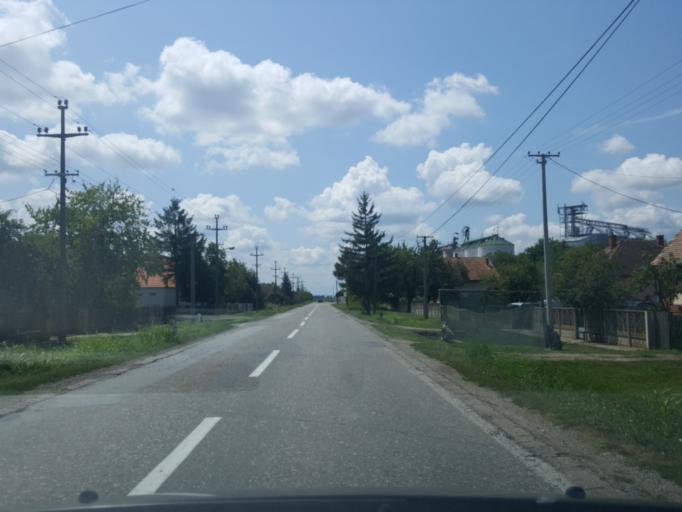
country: RS
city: Glusci
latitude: 44.8773
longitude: 19.5539
